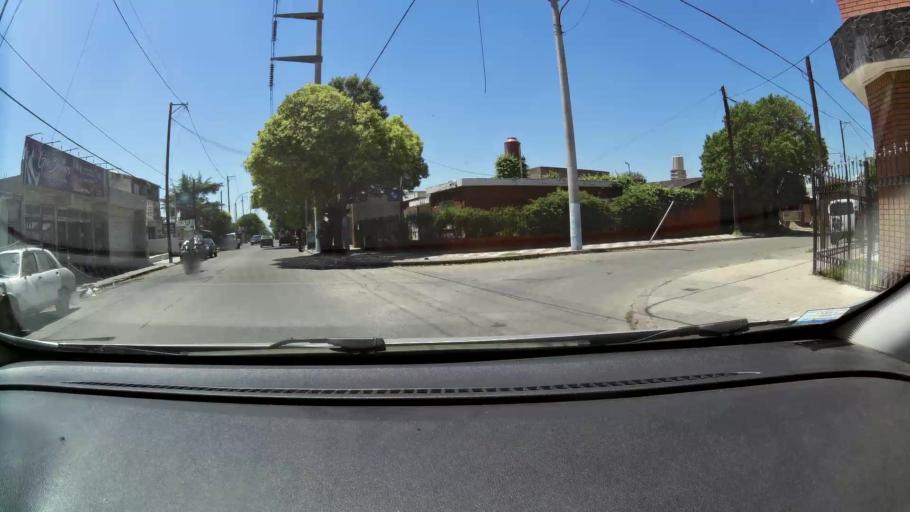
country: AR
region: Cordoba
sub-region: Departamento de Capital
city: Cordoba
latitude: -31.4276
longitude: -64.1255
